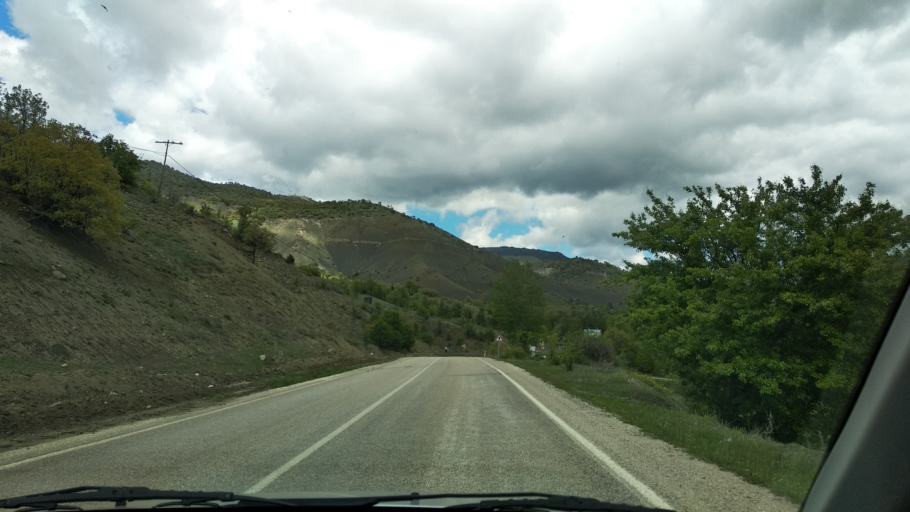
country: TR
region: Bolu
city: Seben
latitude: 40.4245
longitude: 31.5862
